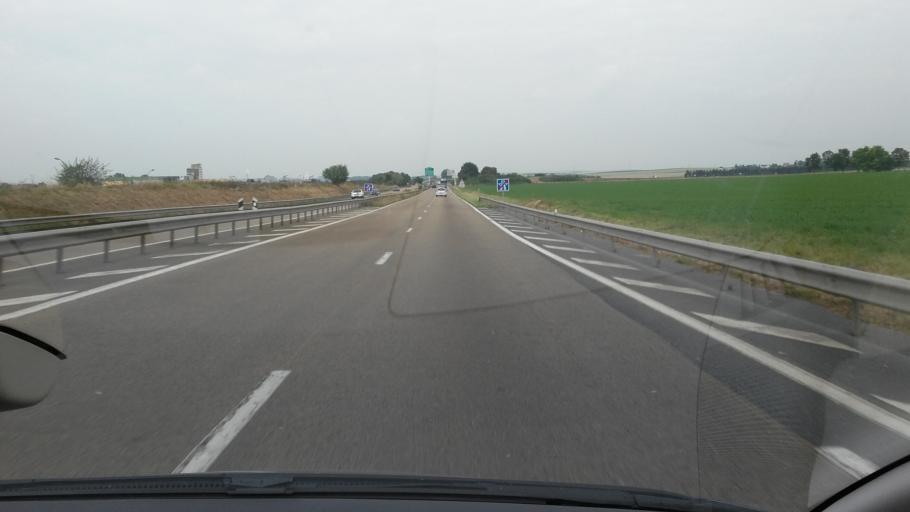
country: FR
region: Champagne-Ardenne
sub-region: Departement de la Marne
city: Witry-les-Reims
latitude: 49.3090
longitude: 4.1438
